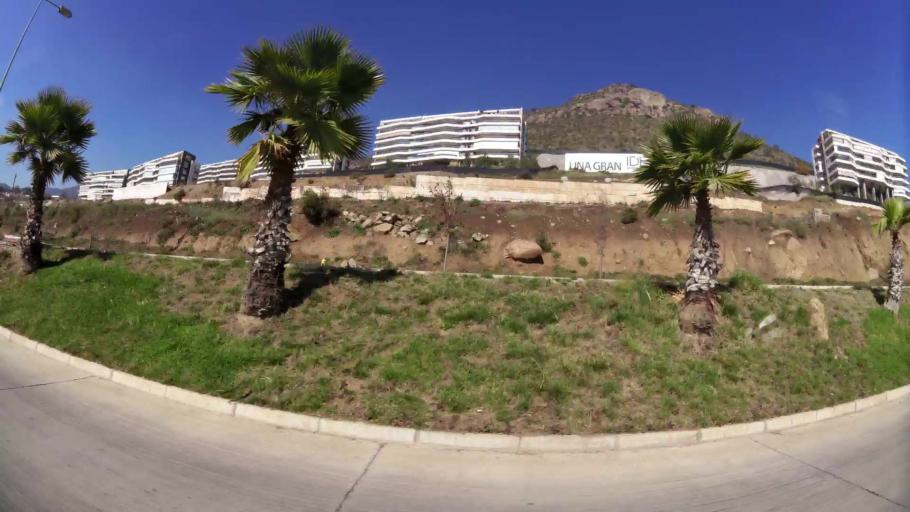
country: CL
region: Santiago Metropolitan
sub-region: Provincia de Santiago
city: Villa Presidente Frei, Nunoa, Santiago, Chile
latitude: -33.4127
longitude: -70.5062
